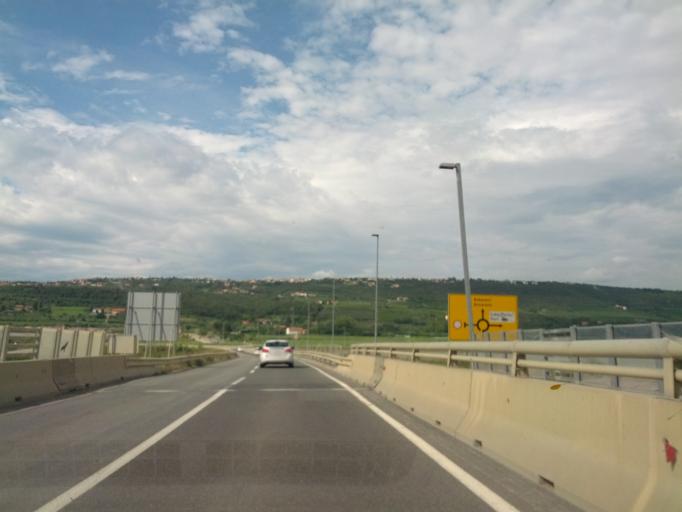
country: SI
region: Koper-Capodistria
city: Hrvatini
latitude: 45.5594
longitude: 13.7573
